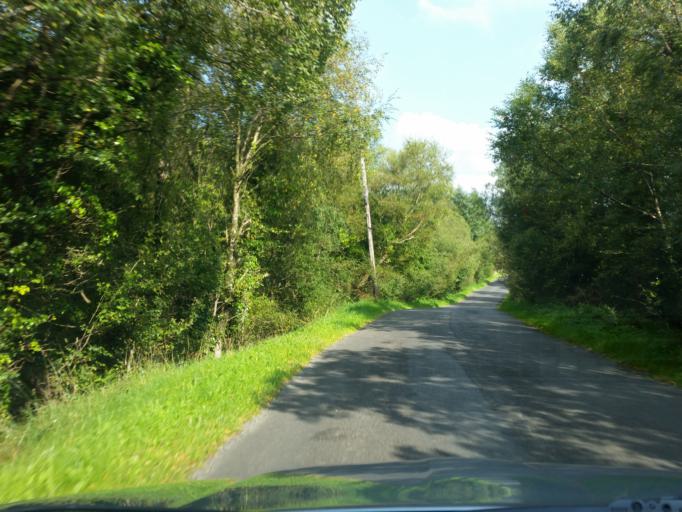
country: GB
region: Northern Ireland
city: Ballinamallard
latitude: 54.3386
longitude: -7.5324
